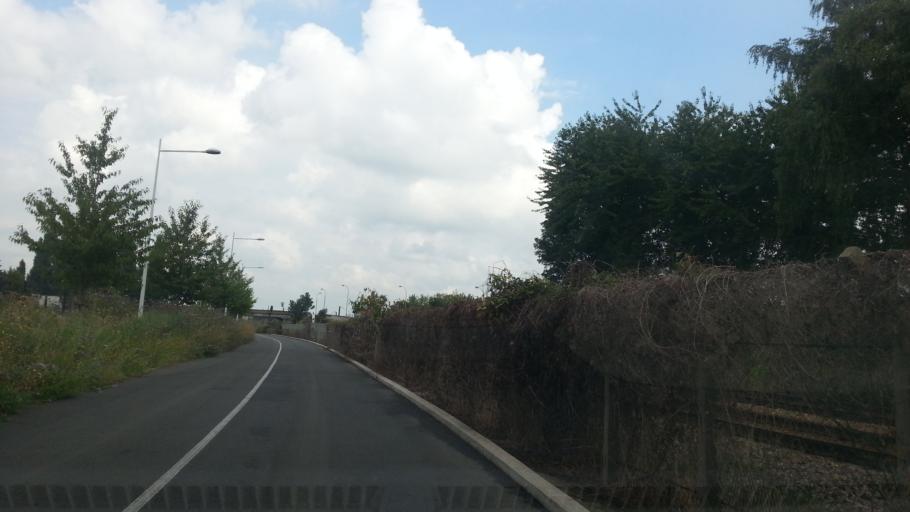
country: FR
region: Picardie
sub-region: Departement de l'Oise
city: Nogent-sur-Oise
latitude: 49.2570
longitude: 2.4593
